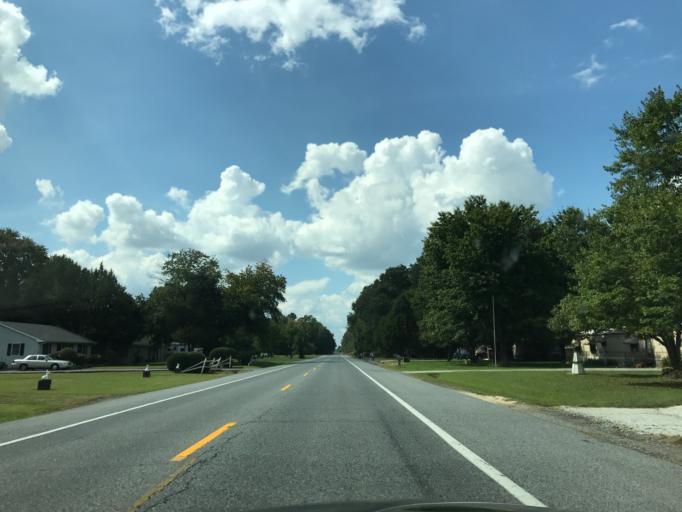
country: US
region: Delaware
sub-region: Kent County
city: Clayton
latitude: 39.1960
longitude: -75.7907
